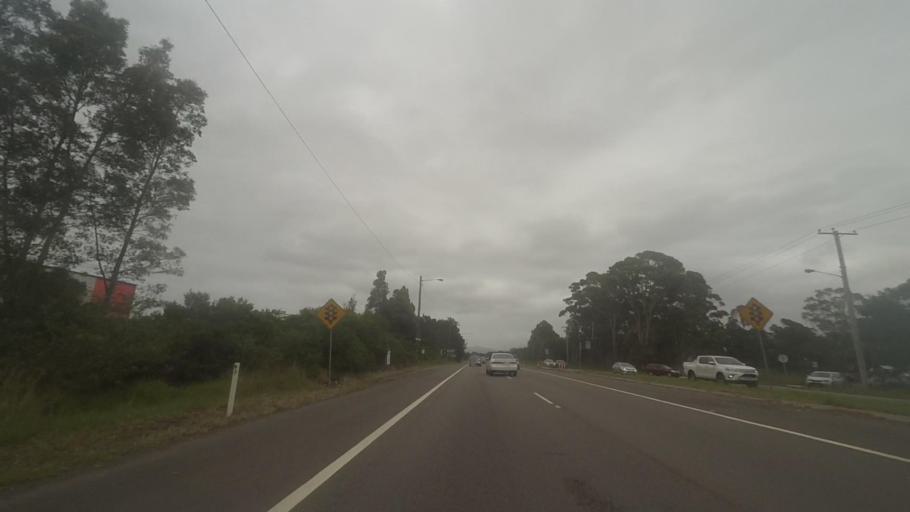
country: AU
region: New South Wales
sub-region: Newcastle
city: Beresfield
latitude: -32.8149
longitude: 151.6998
